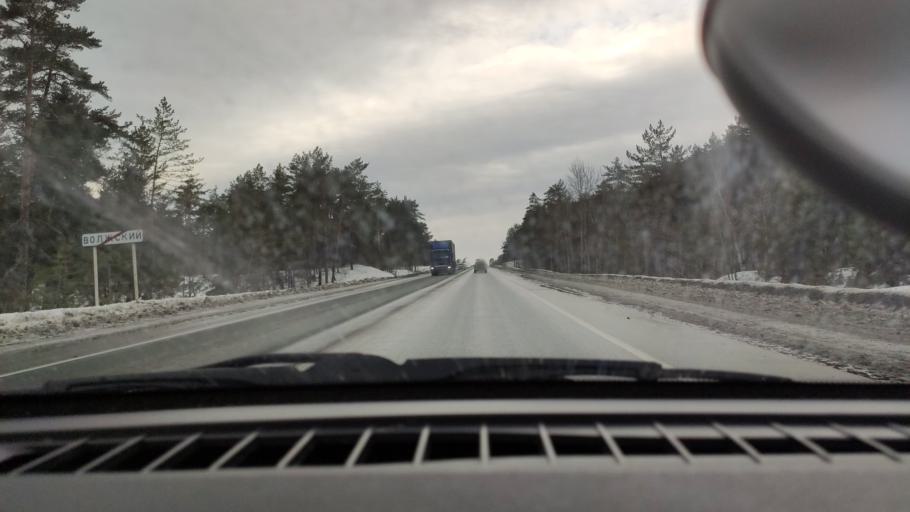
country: RU
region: Samara
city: Volzhskiy
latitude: 53.4408
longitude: 50.1069
